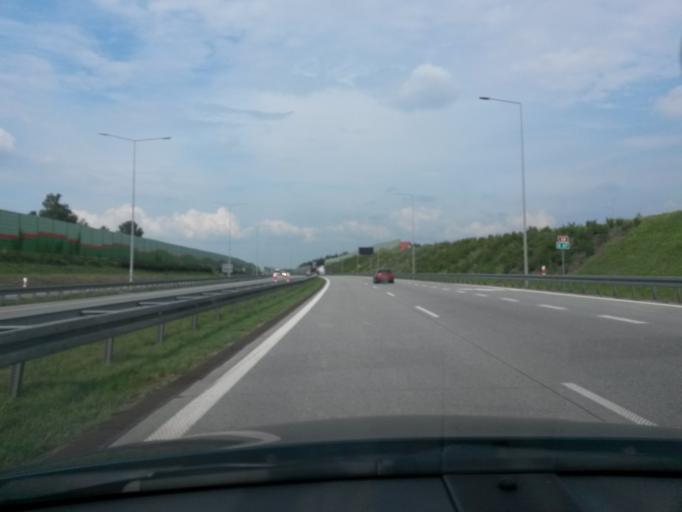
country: PL
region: Lodz Voivodeship
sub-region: Powiat tomaszowski
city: Tomaszow Mazowiecki
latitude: 51.5252
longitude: 19.9400
